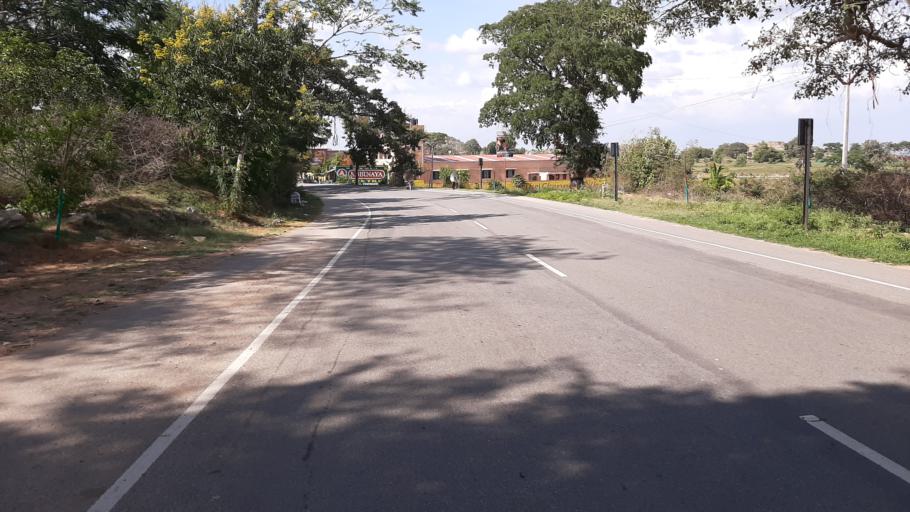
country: IN
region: Tamil Nadu
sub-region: Krishnagiri
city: Denkanikota
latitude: 12.5503
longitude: 77.7861
